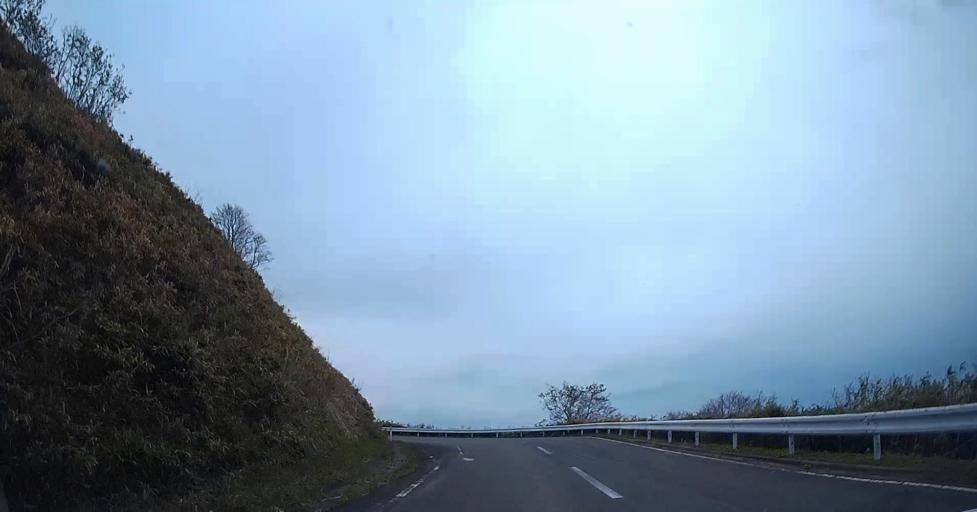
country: JP
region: Aomori
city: Shimokizukuri
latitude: 41.2133
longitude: 140.3560
